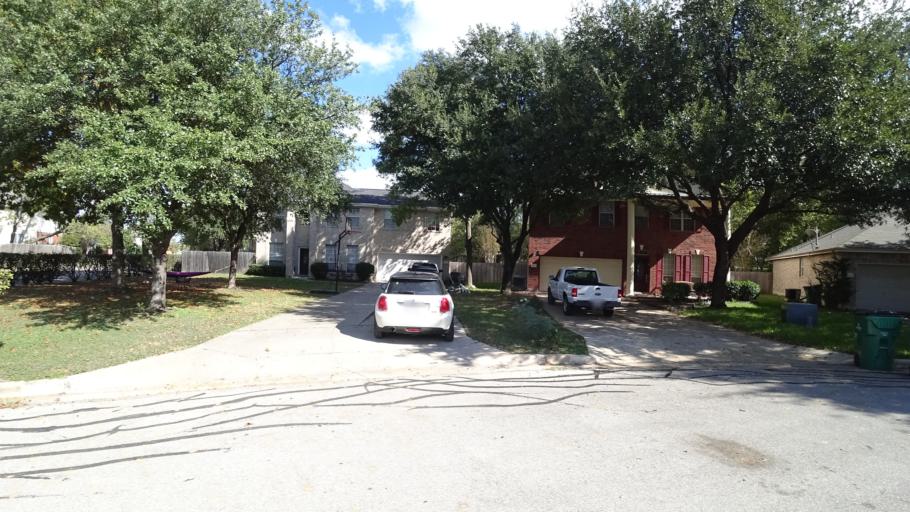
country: US
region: Texas
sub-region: Travis County
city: Windemere
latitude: 30.4572
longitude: -97.6549
